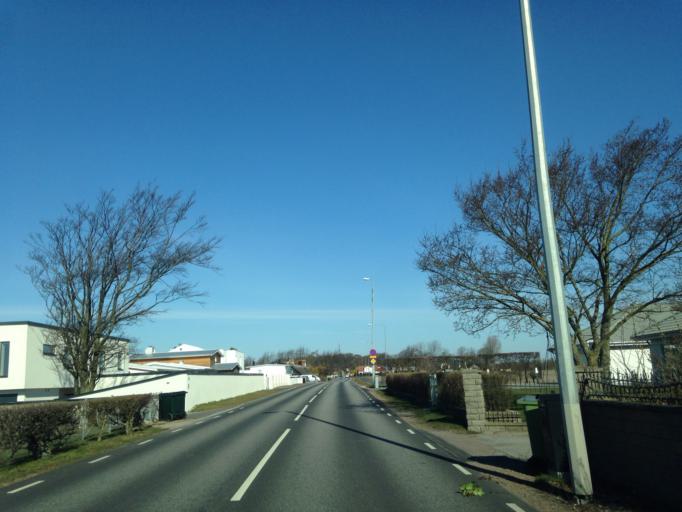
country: SE
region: Skane
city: Bjarred
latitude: 55.7039
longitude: 13.0415
